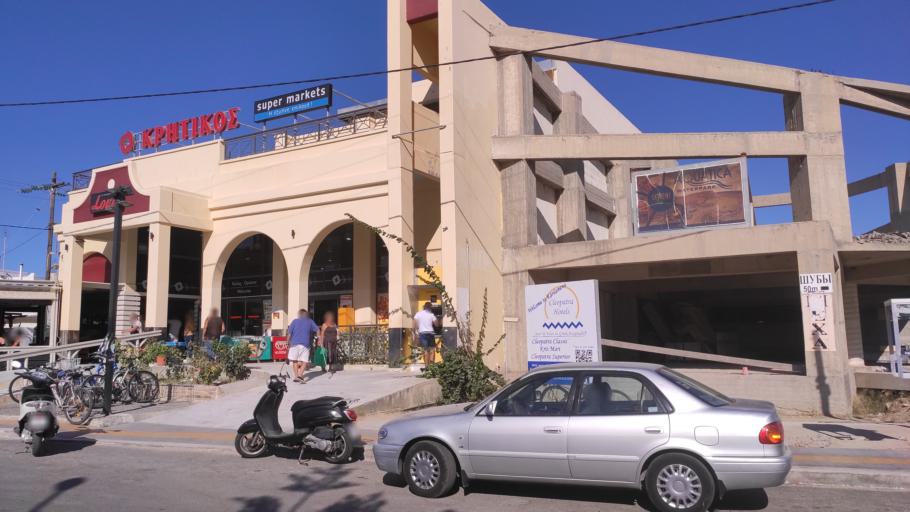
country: GR
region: South Aegean
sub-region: Nomos Dodekanisou
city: Kardamaina
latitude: 36.7832
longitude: 27.1429
